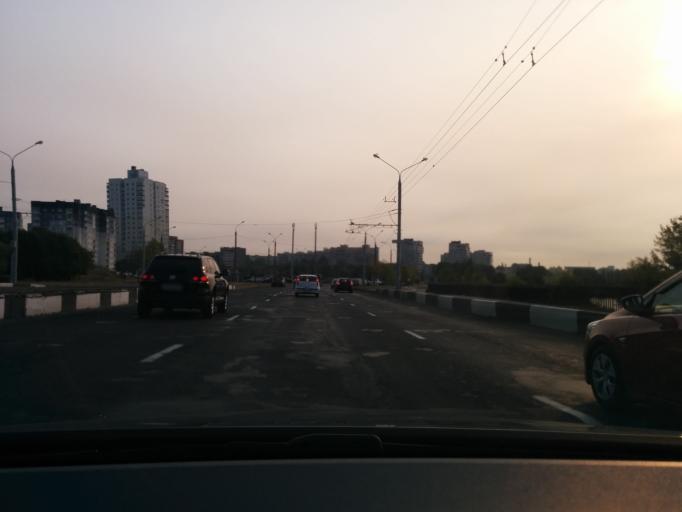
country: BY
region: Minsk
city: Minsk
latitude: 53.8550
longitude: 27.6239
